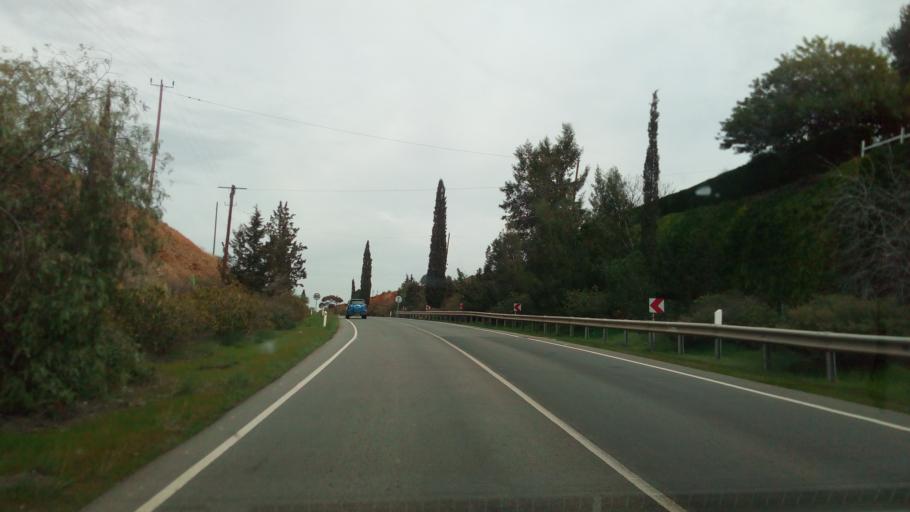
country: CY
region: Lefkosia
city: Astromeritis
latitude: 35.1071
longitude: 32.9815
